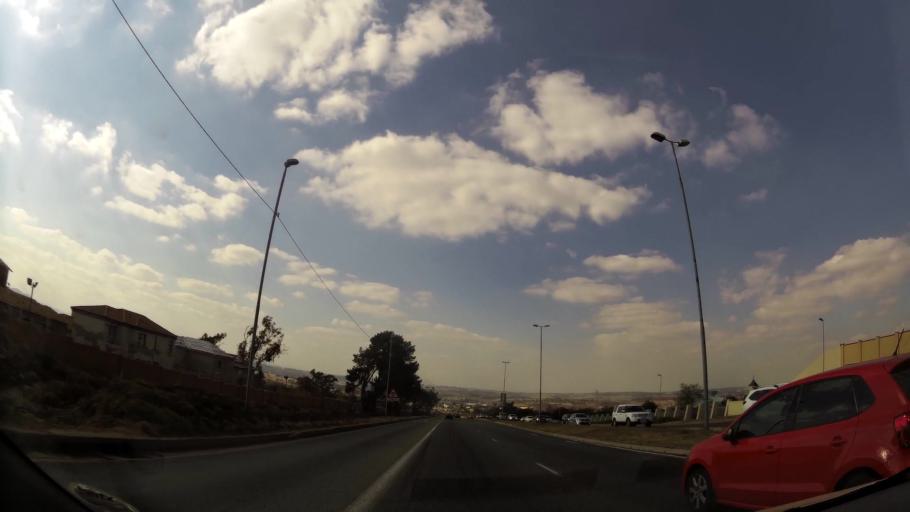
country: ZA
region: Gauteng
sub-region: West Rand District Municipality
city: Muldersdriseloop
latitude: -26.0665
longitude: 27.8245
